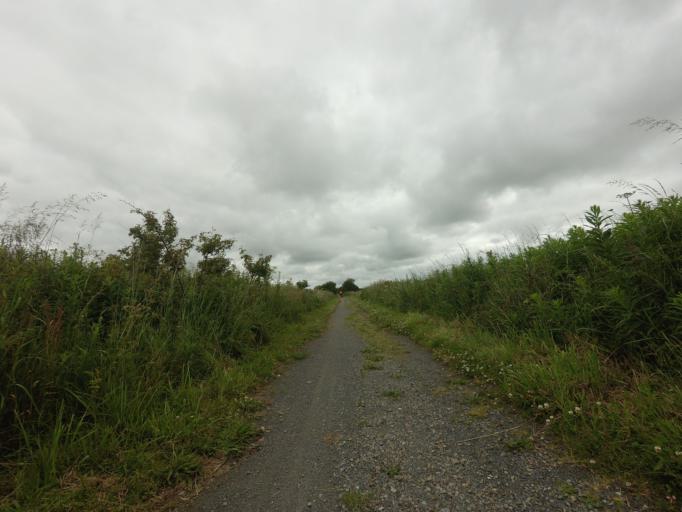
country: GB
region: Scotland
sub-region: Aberdeenshire
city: Ellon
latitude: 57.4711
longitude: -2.1222
